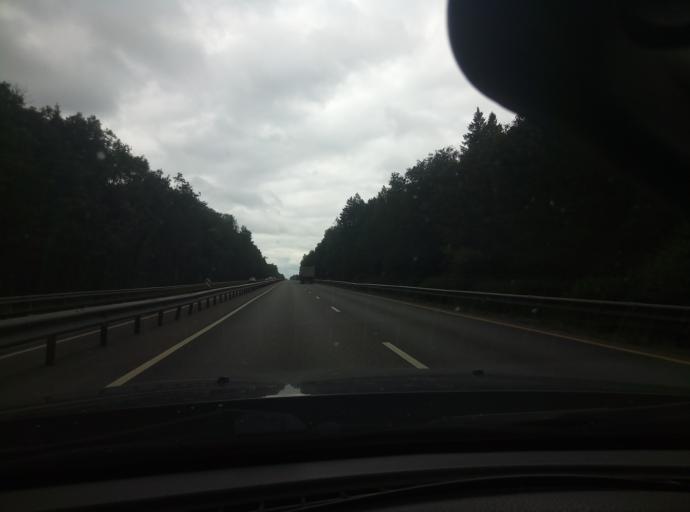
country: RU
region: Kaluga
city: Maloyaroslavets
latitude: 54.9888
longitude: 36.5089
